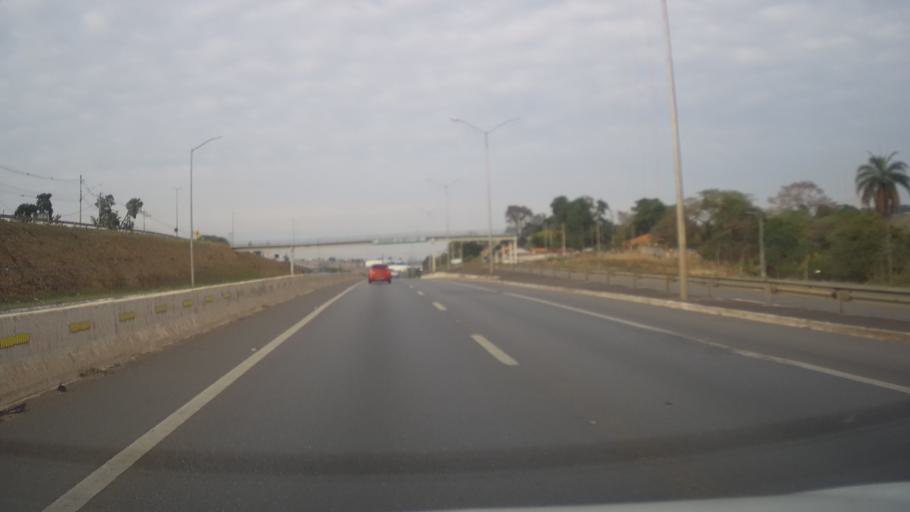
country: BR
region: Minas Gerais
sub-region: Vespasiano
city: Vespasiano
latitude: -19.7233
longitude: -43.9343
